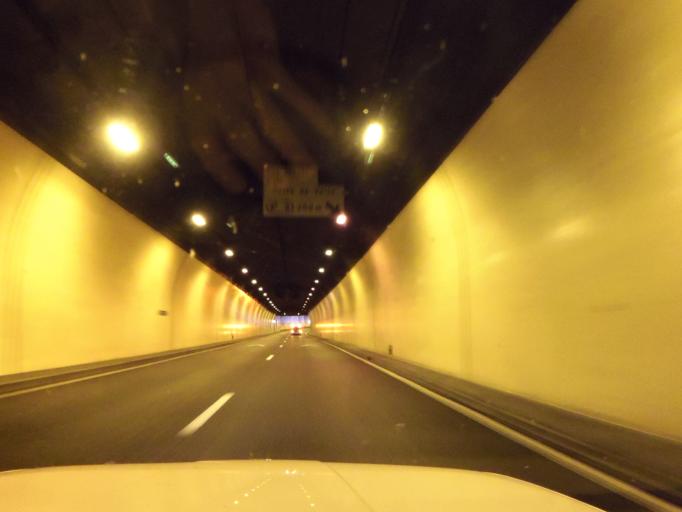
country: FR
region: Rhone-Alpes
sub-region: Departement du Rhone
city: Ecully
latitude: 45.7888
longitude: 4.8064
